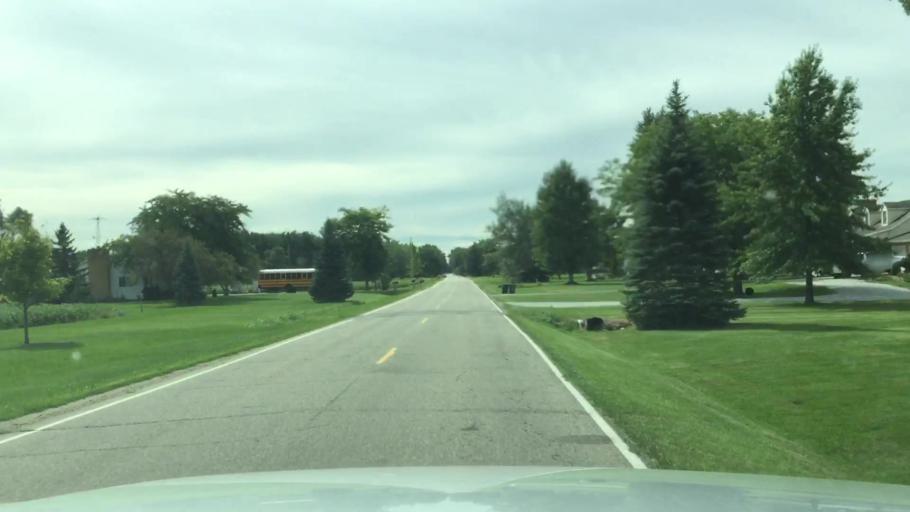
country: US
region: Michigan
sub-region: Genesee County
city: Montrose
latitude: 43.1115
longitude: -83.9880
